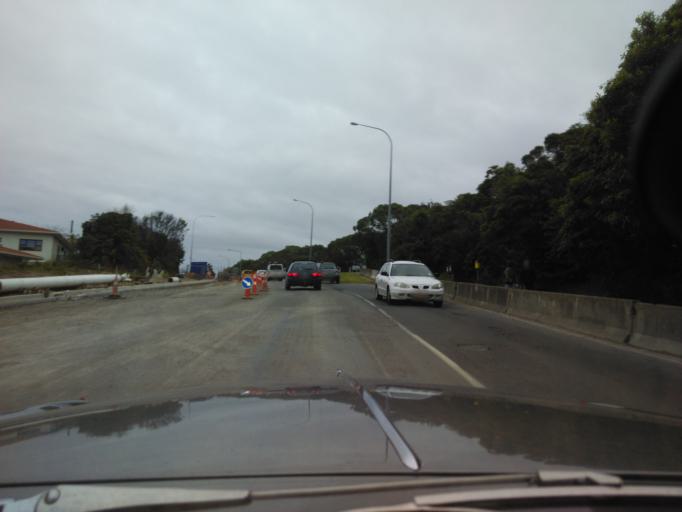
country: NZ
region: Auckland
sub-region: Auckland
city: Rothesay Bay
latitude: -36.7325
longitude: 174.6933
